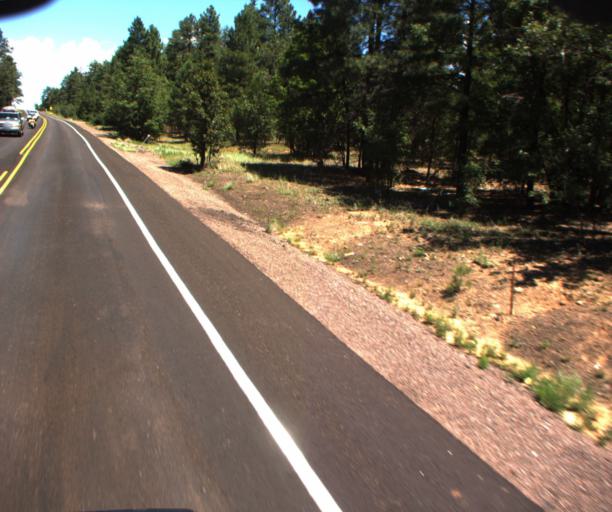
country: US
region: Arizona
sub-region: Navajo County
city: Show Low
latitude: 34.2009
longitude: -110.0837
